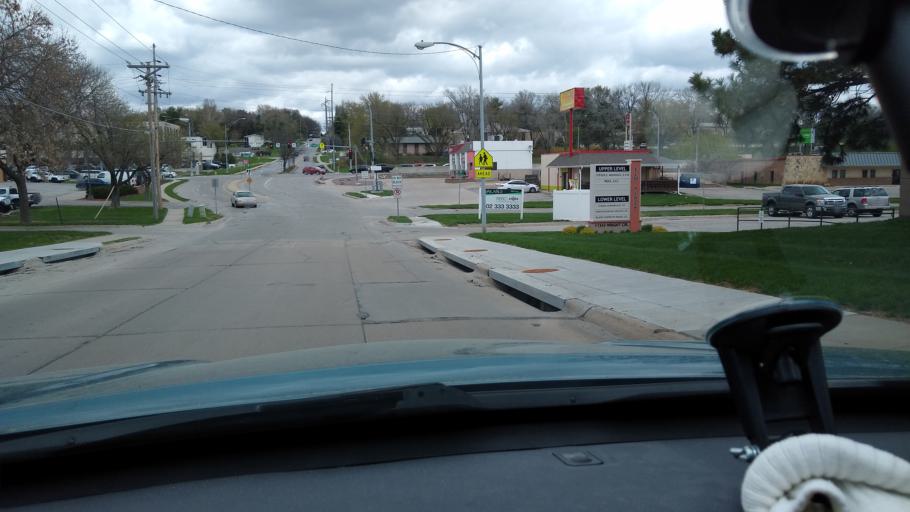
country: US
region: Nebraska
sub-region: Douglas County
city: Ralston
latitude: 41.2328
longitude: -96.0910
